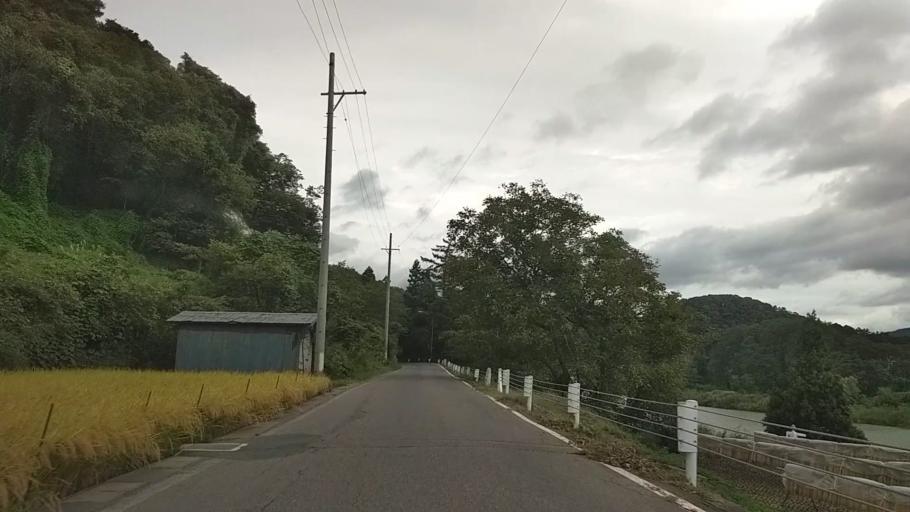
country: JP
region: Nagano
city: Nakano
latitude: 36.7985
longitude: 138.3438
